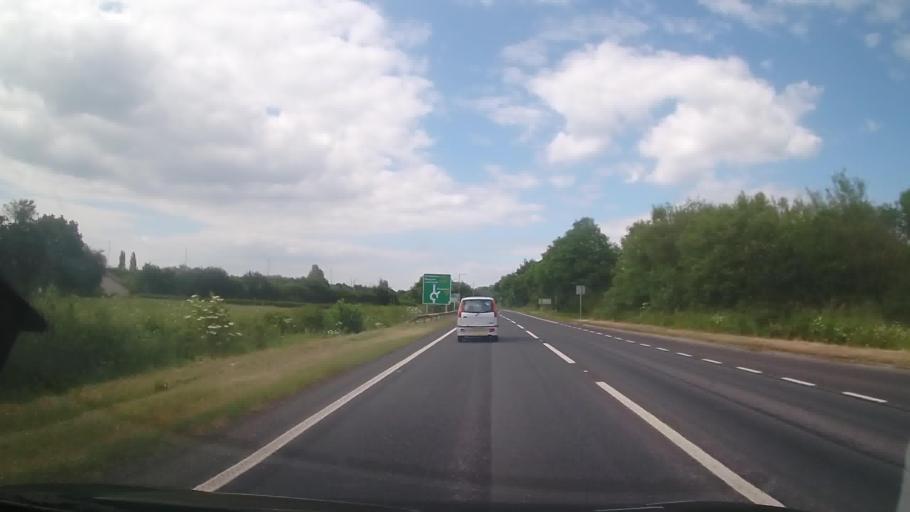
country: GB
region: England
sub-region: Herefordshire
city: Leominster
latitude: 52.2187
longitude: -2.7261
